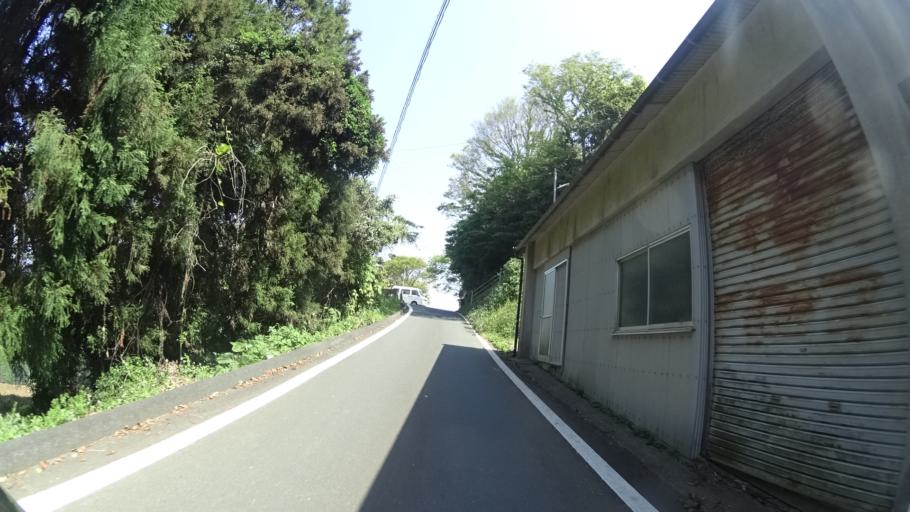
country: JP
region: Ehime
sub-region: Nishiuwa-gun
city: Ikata-cho
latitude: 33.3689
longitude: 132.0494
